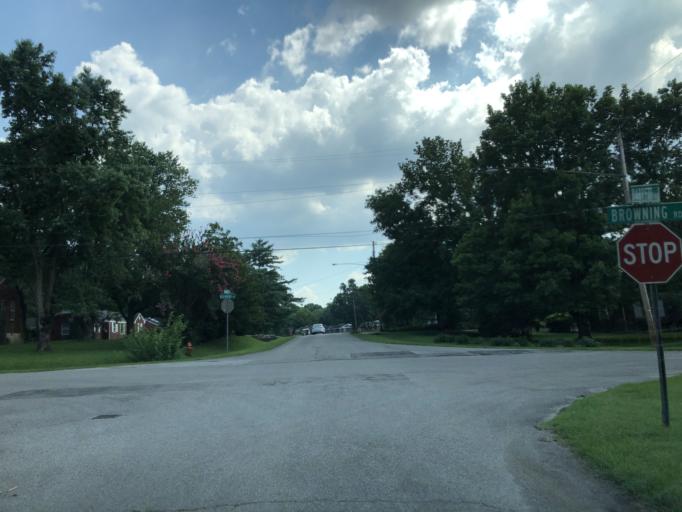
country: US
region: Tennessee
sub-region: Davidson County
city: Oak Hill
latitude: 36.1218
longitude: -86.7206
